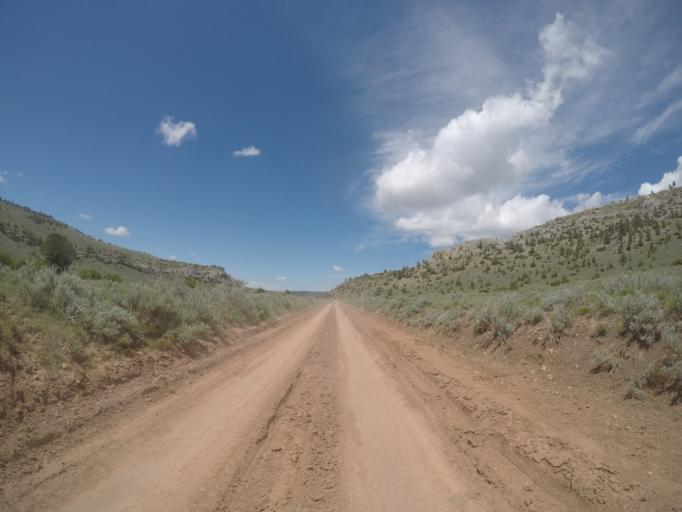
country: US
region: Wyoming
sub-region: Big Horn County
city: Lovell
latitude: 45.2336
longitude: -108.6152
